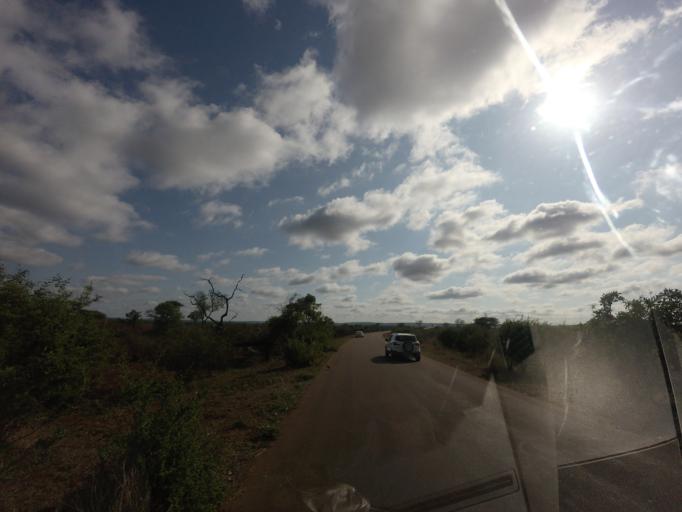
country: ZA
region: Mpumalanga
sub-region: Ehlanzeni District
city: Komatipoort
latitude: -25.1682
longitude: 31.9206
